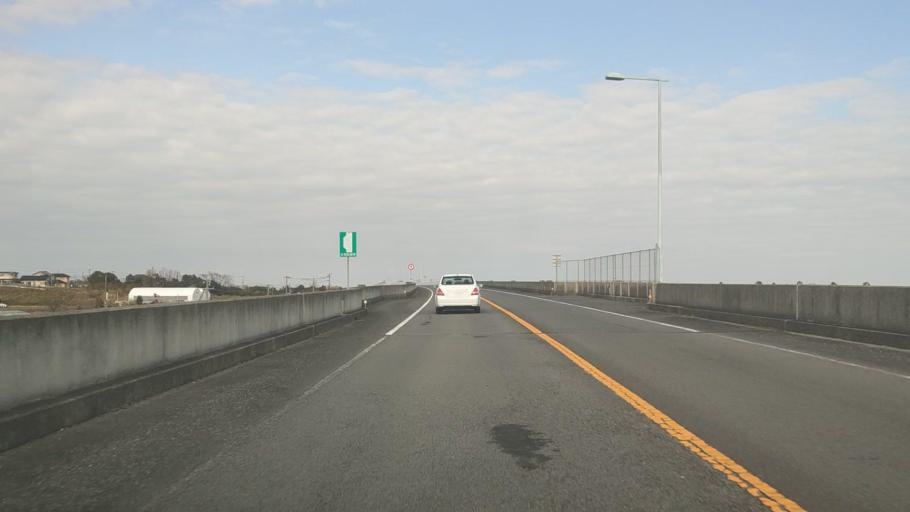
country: JP
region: Nagasaki
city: Shimabara
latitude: 32.7371
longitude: 130.3704
